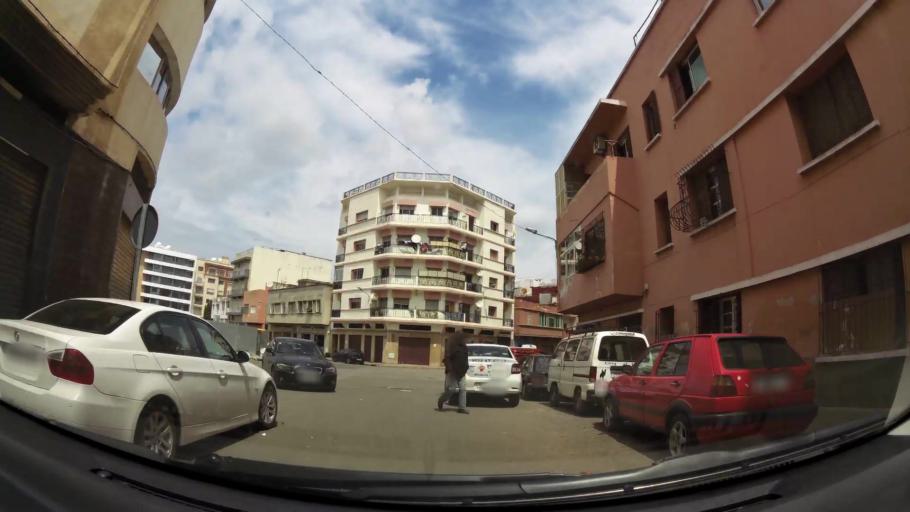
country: MA
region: Grand Casablanca
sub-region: Casablanca
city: Casablanca
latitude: 33.5673
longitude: -7.6541
